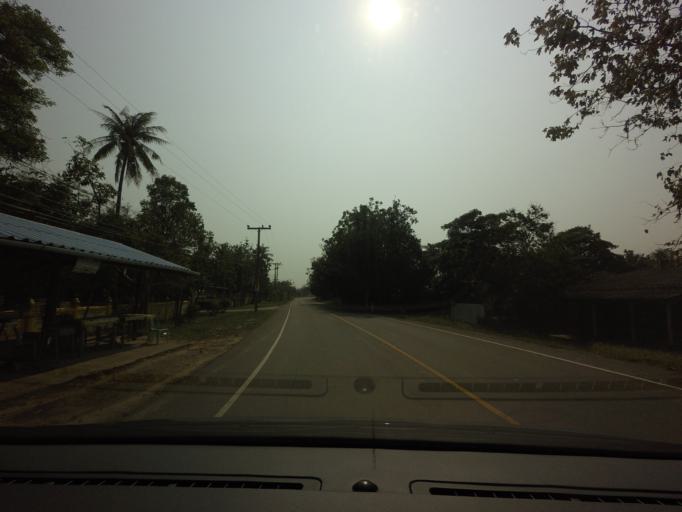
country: TH
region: Prachuap Khiri Khan
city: Kui Buri
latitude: 12.0424
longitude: 99.9050
